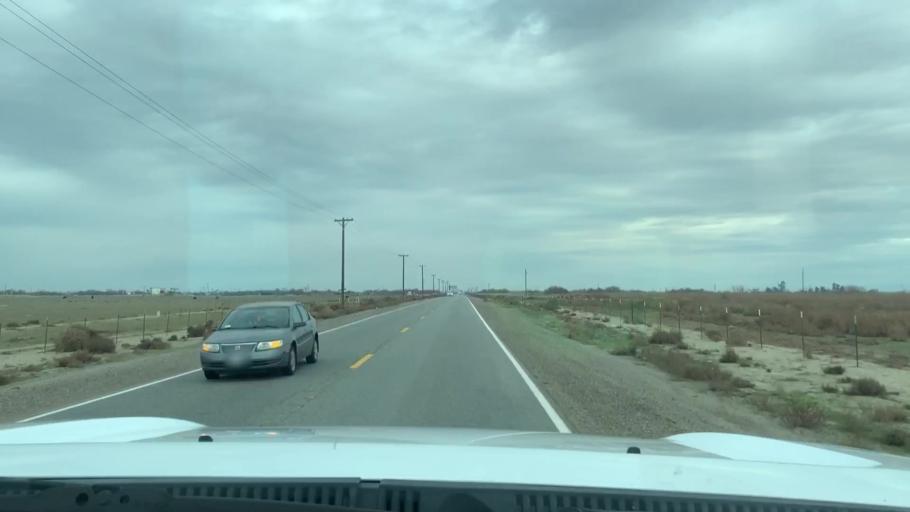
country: US
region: California
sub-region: Kern County
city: Rosedale
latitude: 35.3119
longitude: -119.2524
